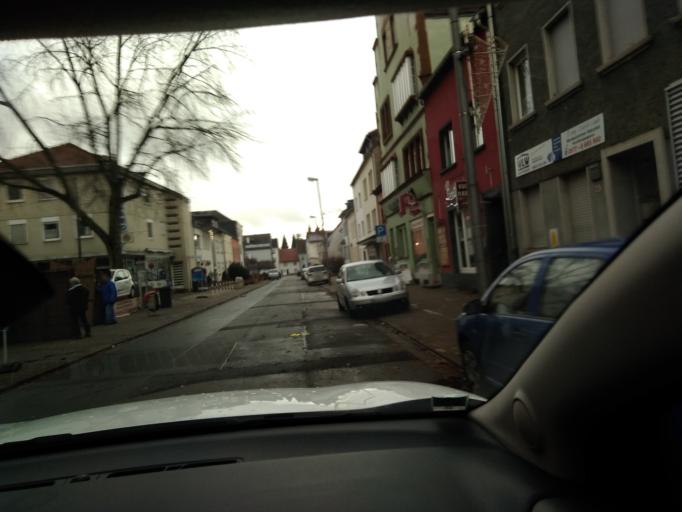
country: DE
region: Saarland
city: Saarlouis
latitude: 49.3323
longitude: 6.7482
